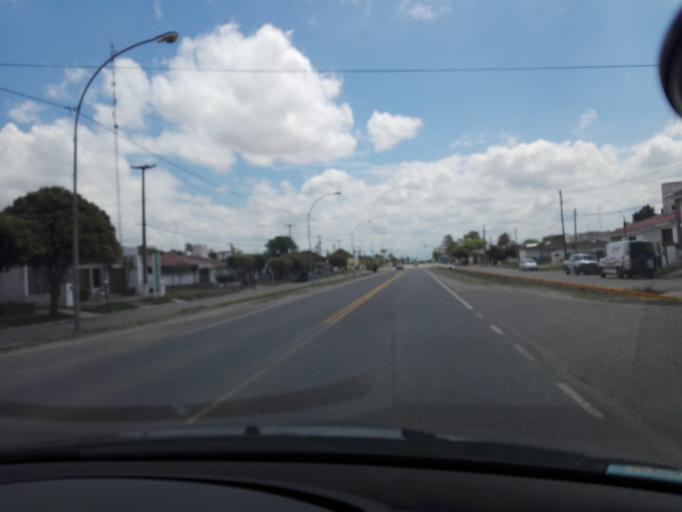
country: AR
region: Cordoba
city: Toledo
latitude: -31.6490
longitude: -64.0859
